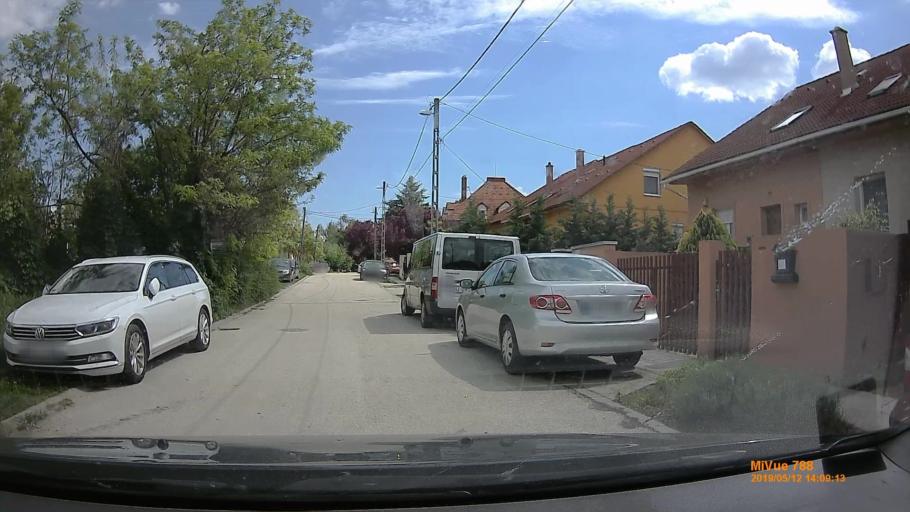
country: HU
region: Budapest
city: Budapest XVII. keruelet
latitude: 47.4886
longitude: 19.2826
